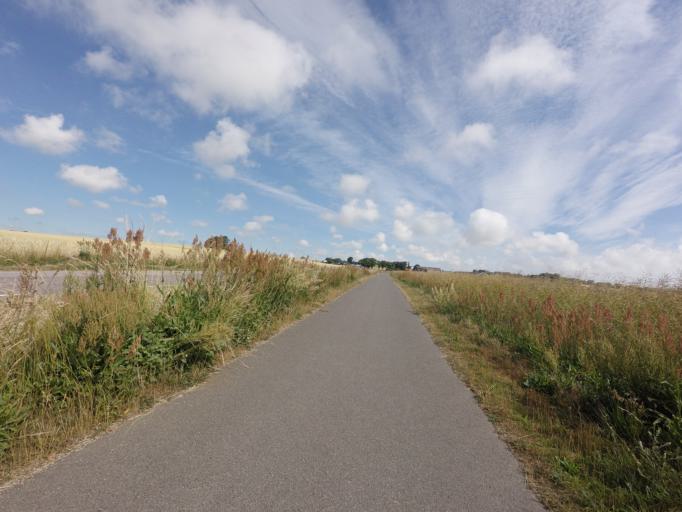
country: SE
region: Skane
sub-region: Simrishamns Kommun
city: Simrishamn
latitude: 55.4795
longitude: 14.2842
